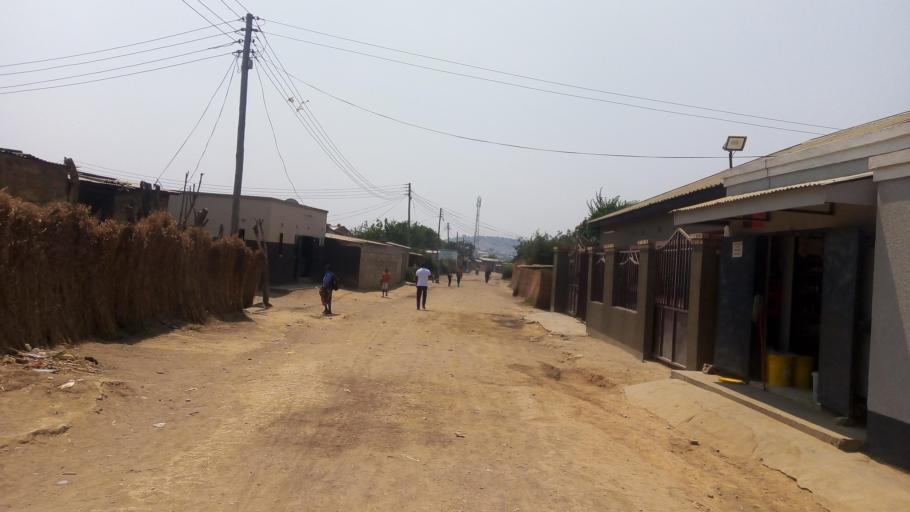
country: ZM
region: Lusaka
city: Lusaka
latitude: -15.4430
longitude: 28.3765
